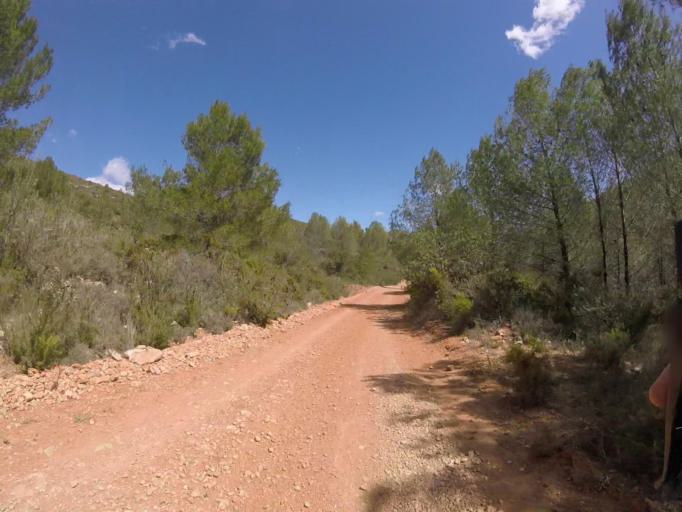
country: ES
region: Valencia
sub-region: Provincia de Castello
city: Cabanes
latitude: 40.1636
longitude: 0.1143
